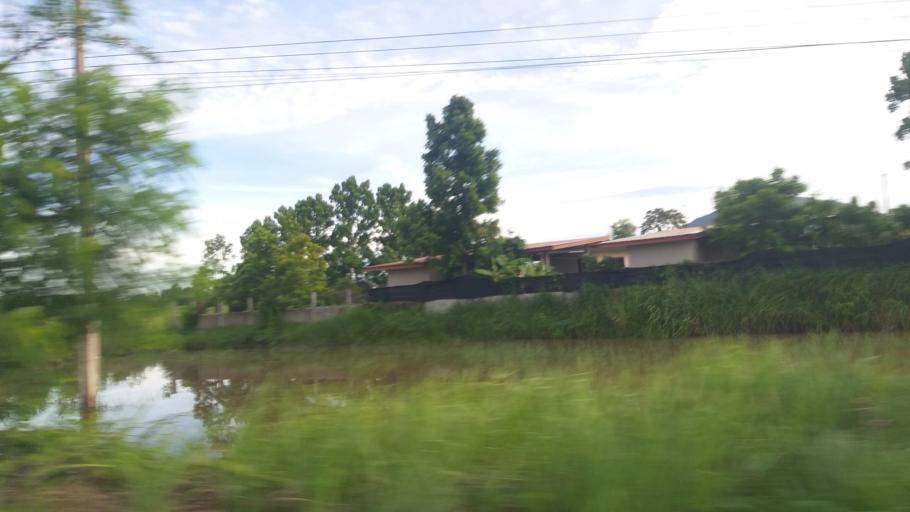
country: TH
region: Chaiyaphum
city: Phu Khiao
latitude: 16.3343
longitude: 102.2284
